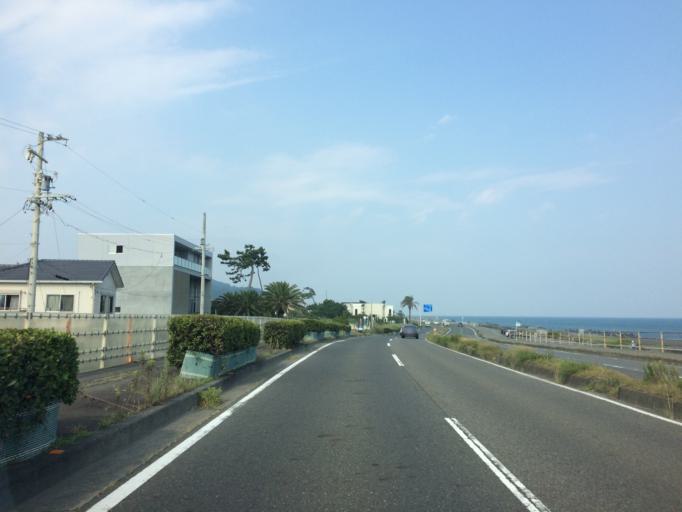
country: JP
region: Shizuoka
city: Shizuoka-shi
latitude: 34.9446
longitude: 138.4177
